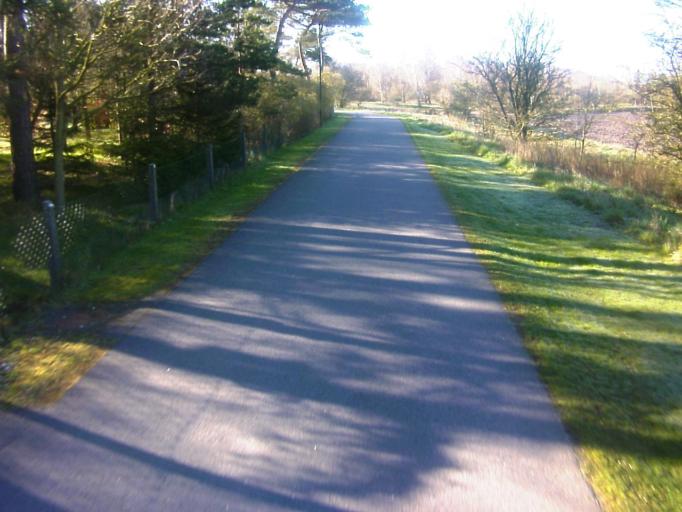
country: SE
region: Skane
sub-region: Kavlinge Kommun
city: Hofterup
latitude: 55.8134
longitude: 12.9686
